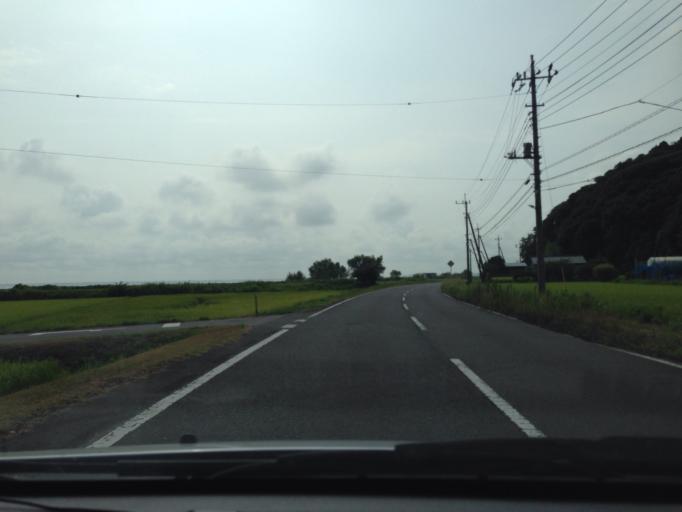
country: JP
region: Ibaraki
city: Inashiki
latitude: 36.0253
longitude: 140.3517
